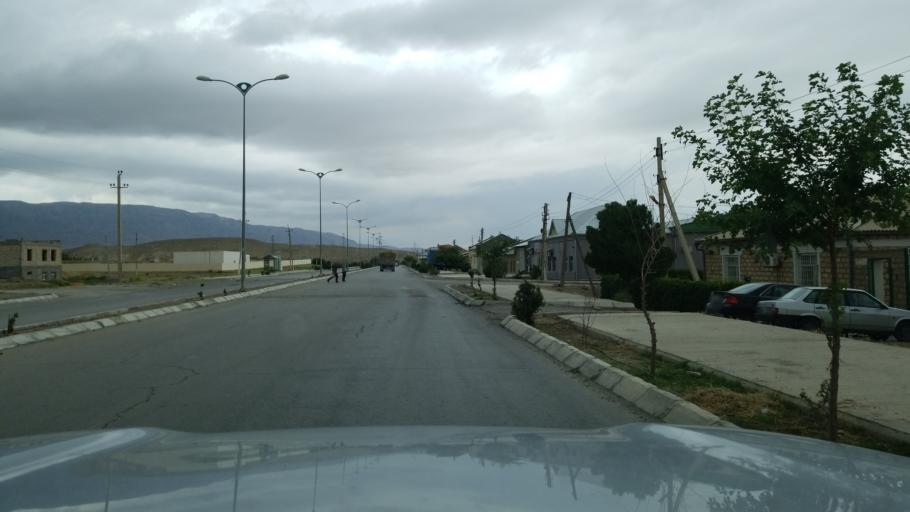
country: TM
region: Balkan
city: Serdar
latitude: 38.9607
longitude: 56.2862
